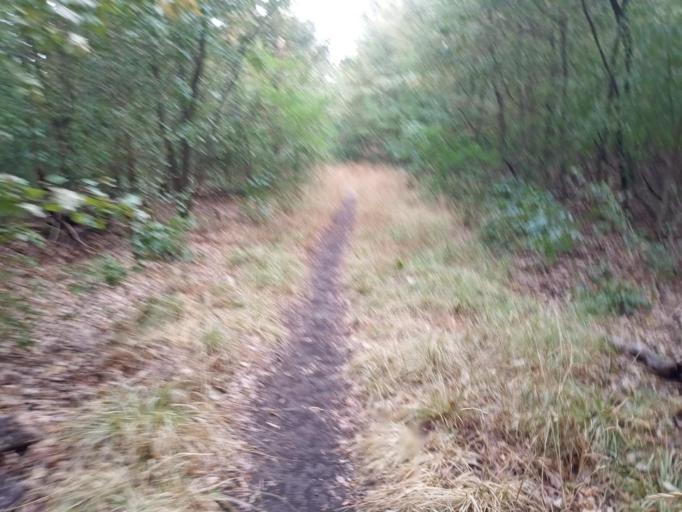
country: HU
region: Pest
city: Pilisborosjeno
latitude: 47.6235
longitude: 19.0012
